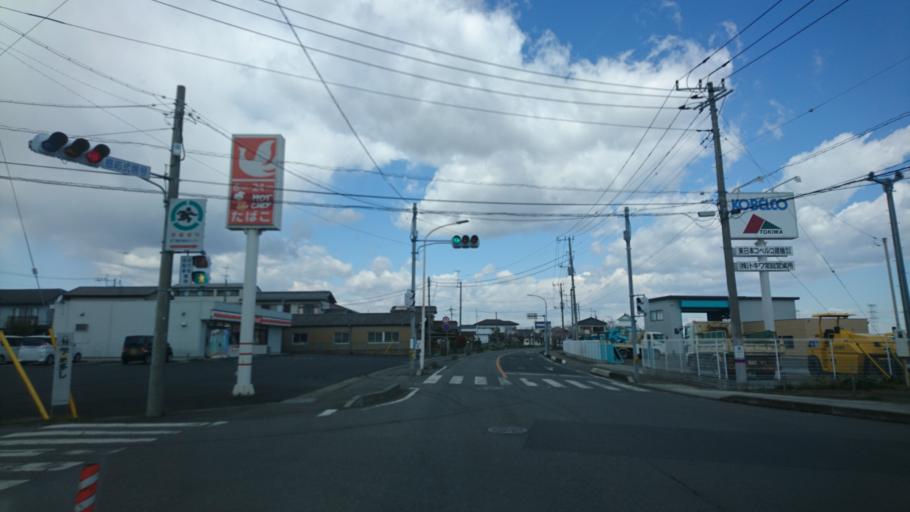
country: JP
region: Ibaraki
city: Ishige
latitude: 36.1142
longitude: 139.9787
